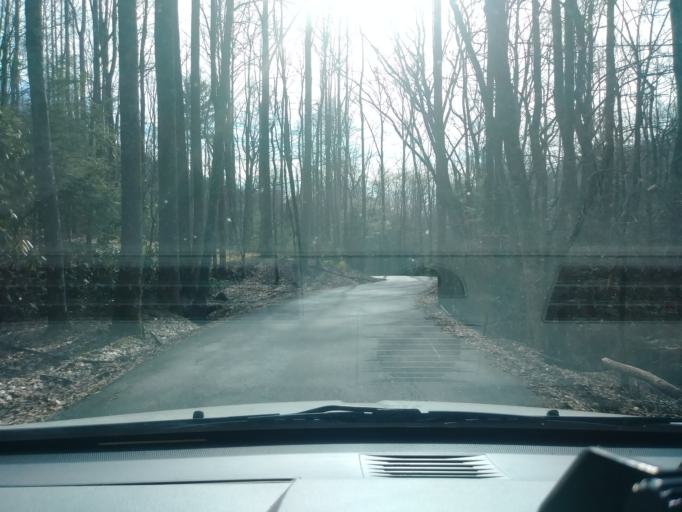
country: US
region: Tennessee
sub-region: Greene County
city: Tusculum
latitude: 36.0251
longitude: -82.7361
